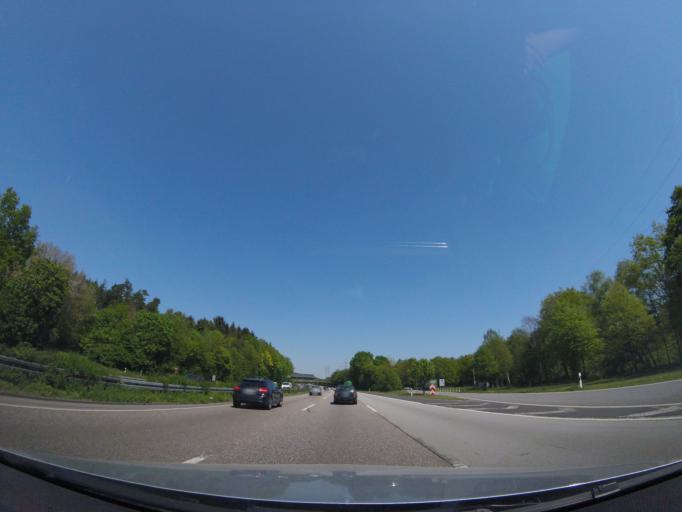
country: DE
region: Hesse
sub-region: Regierungsbezirk Darmstadt
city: Offenbach
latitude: 50.0769
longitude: 8.7357
